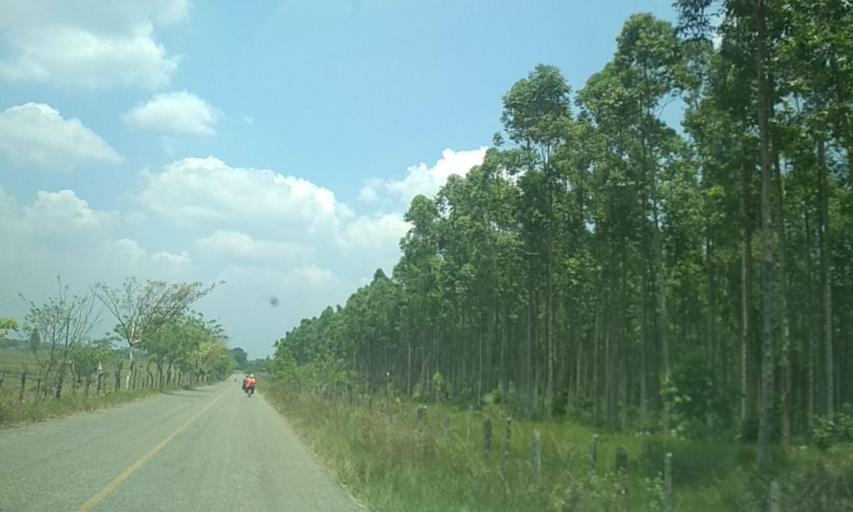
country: MX
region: Tabasco
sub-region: Huimanguillo
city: Francisco Rueda
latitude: 17.8389
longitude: -93.9033
